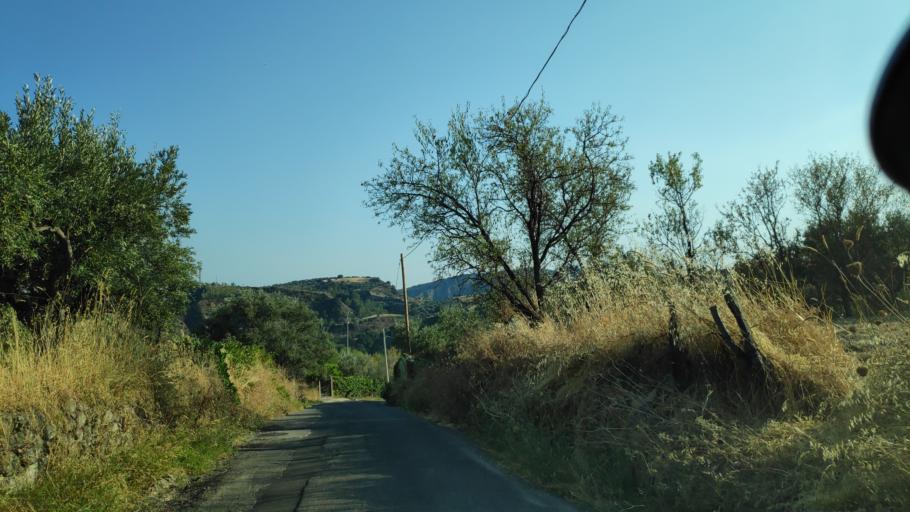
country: IT
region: Calabria
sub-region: Provincia di Catanzaro
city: Guardavalle
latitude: 38.5095
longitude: 16.5044
